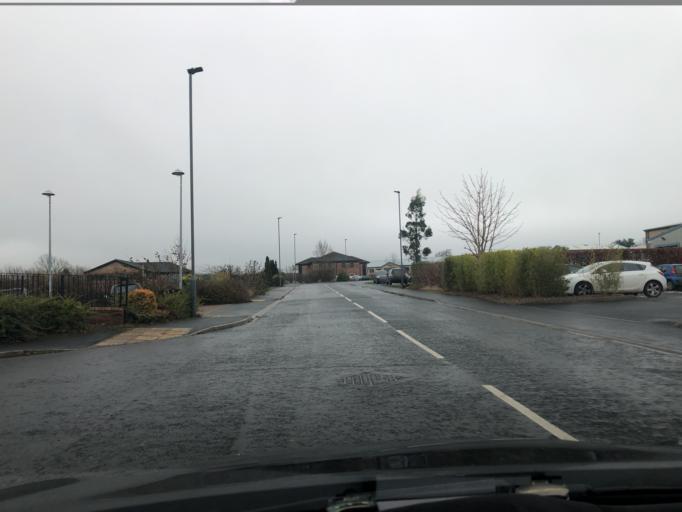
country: GB
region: England
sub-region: North Yorkshire
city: Stokesley
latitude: 54.4628
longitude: -1.1752
